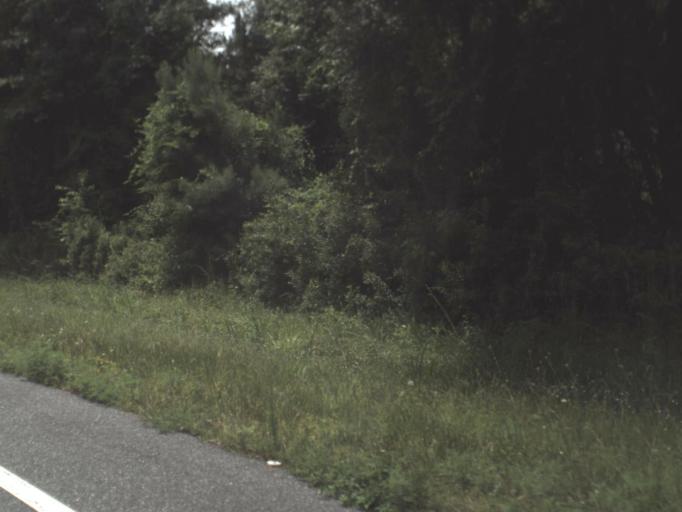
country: US
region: Florida
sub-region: Columbia County
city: Watertown
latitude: 30.1248
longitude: -82.5156
